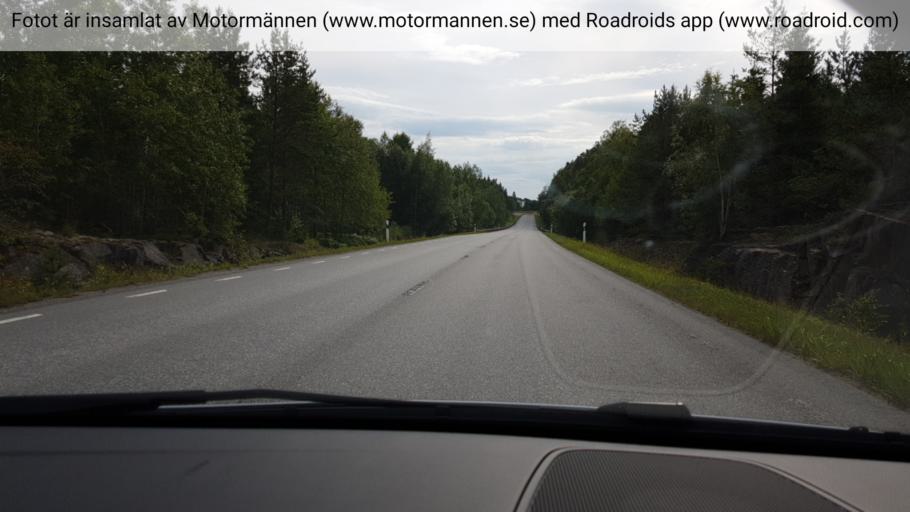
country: SE
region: Uppsala
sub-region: Osthammars Kommun
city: OEsthammar
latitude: 60.2264
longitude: 18.3667
